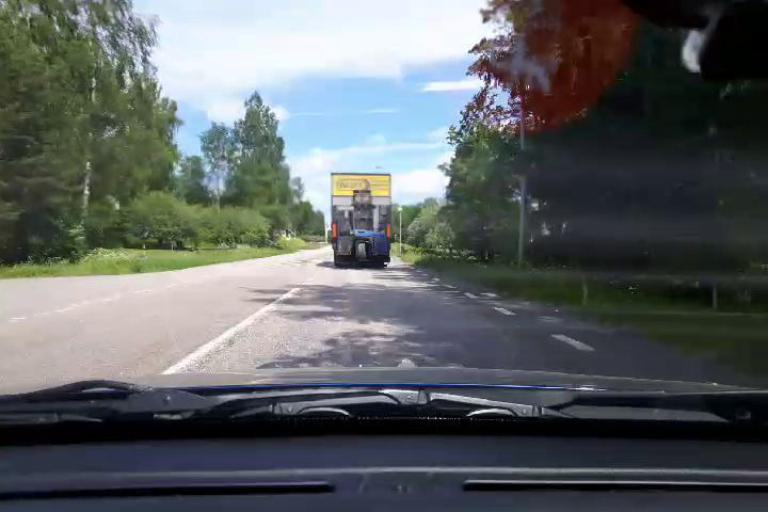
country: SE
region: Uppsala
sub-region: Osthammars Kommun
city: Bjorklinge
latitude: 60.0844
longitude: 17.5486
